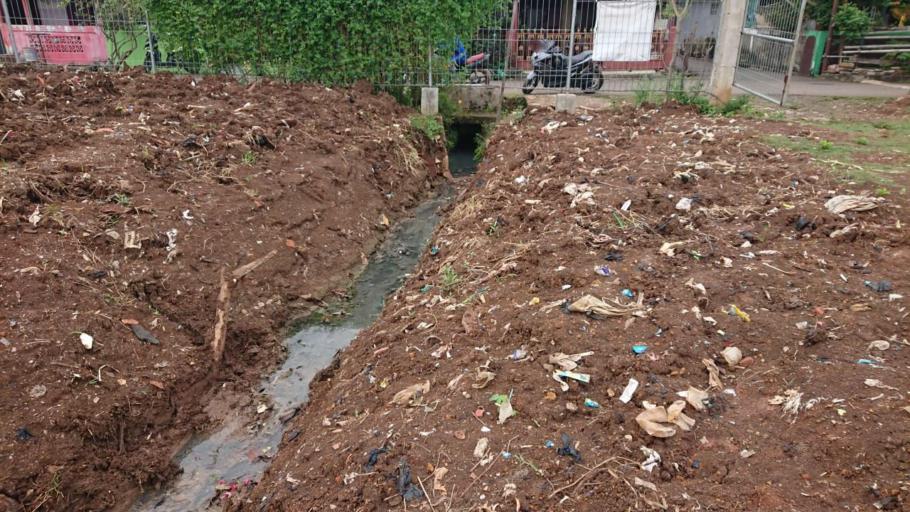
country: ID
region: West Java
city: Depok
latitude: -6.3492
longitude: 106.8230
